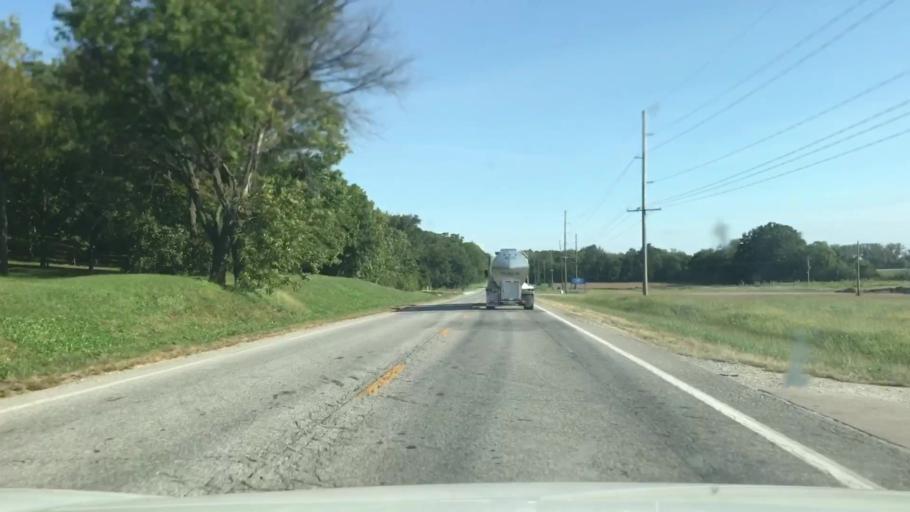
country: US
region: Illinois
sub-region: Adams County
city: Quincy
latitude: 39.8486
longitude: -91.3778
